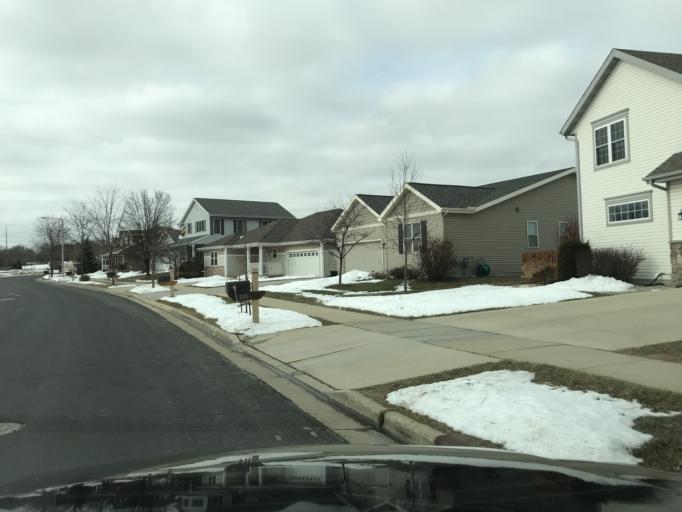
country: US
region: Wisconsin
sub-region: Dane County
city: Cottage Grove
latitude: 43.0960
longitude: -89.2625
